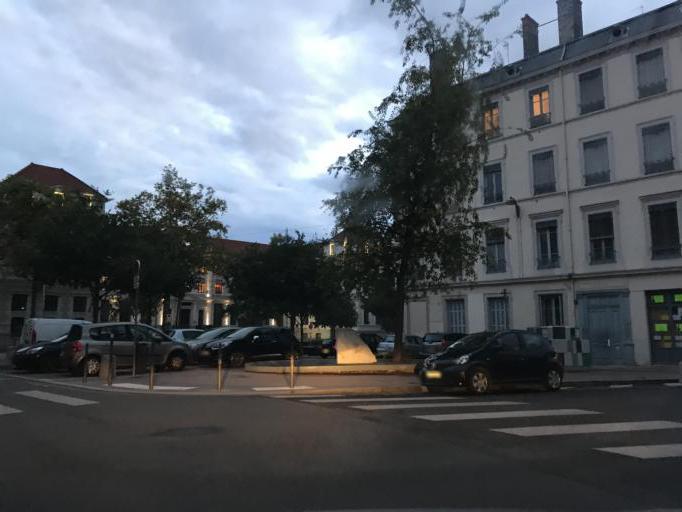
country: FR
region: Rhone-Alpes
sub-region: Departement du Rhone
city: Caluire-et-Cuire
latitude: 45.7745
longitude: 4.8253
